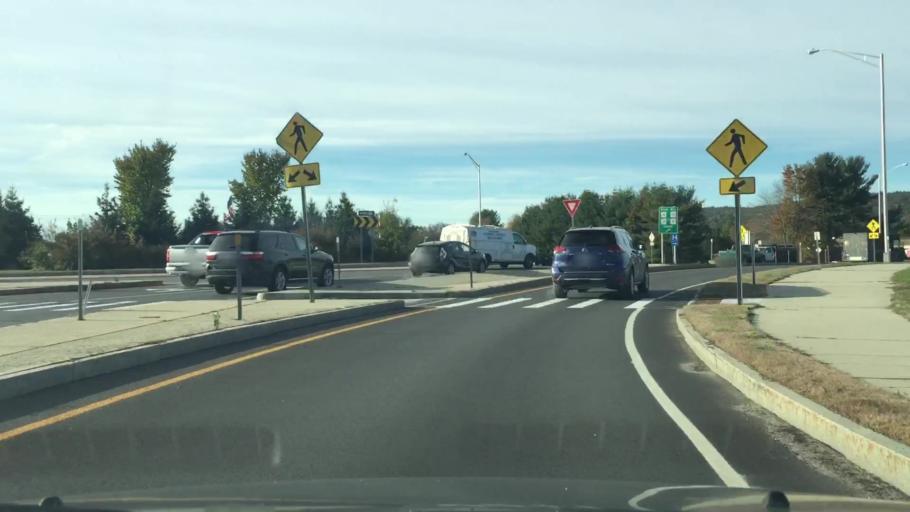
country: US
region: New Hampshire
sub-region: Cheshire County
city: Keene
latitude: 42.9231
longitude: -72.2906
